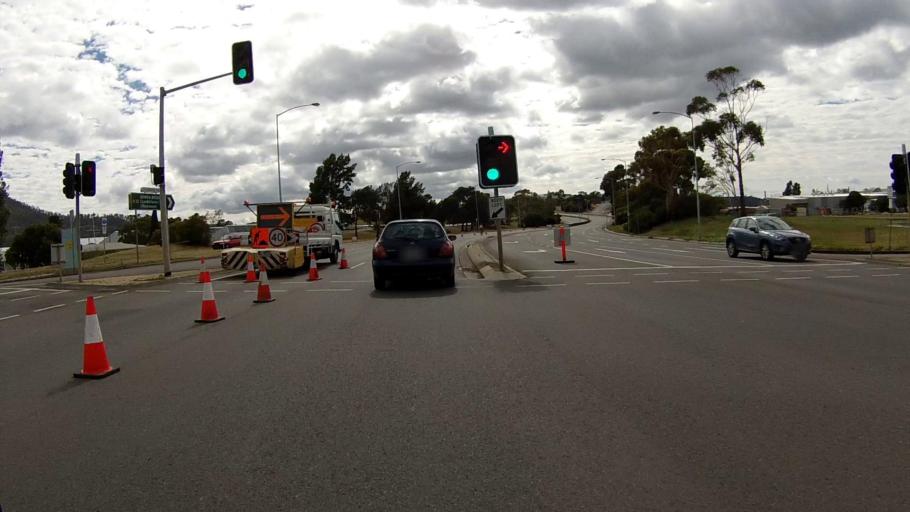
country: AU
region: Tasmania
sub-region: Glenorchy
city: Goodwood
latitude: -42.8233
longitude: 147.2948
